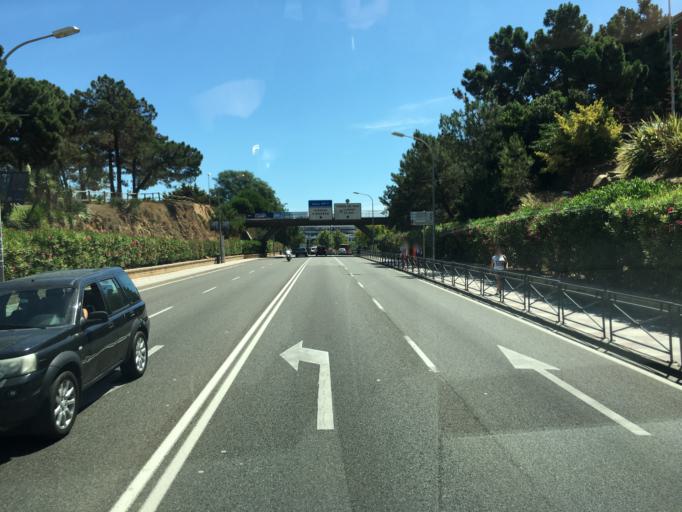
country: ES
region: Catalonia
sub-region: Provincia de Girona
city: Lloret de Mar
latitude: 41.7005
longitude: 2.8356
